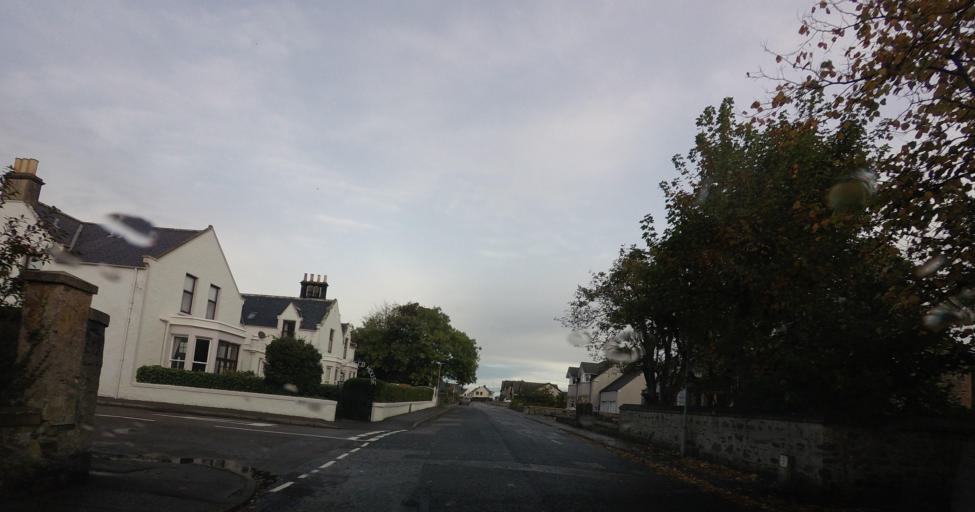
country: GB
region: Scotland
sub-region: Moray
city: Cullen
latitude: 57.6910
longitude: -2.8158
